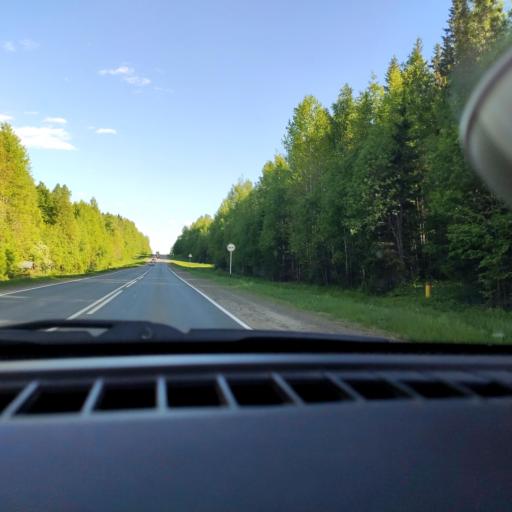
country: RU
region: Perm
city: Perm
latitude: 58.1569
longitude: 56.2499
